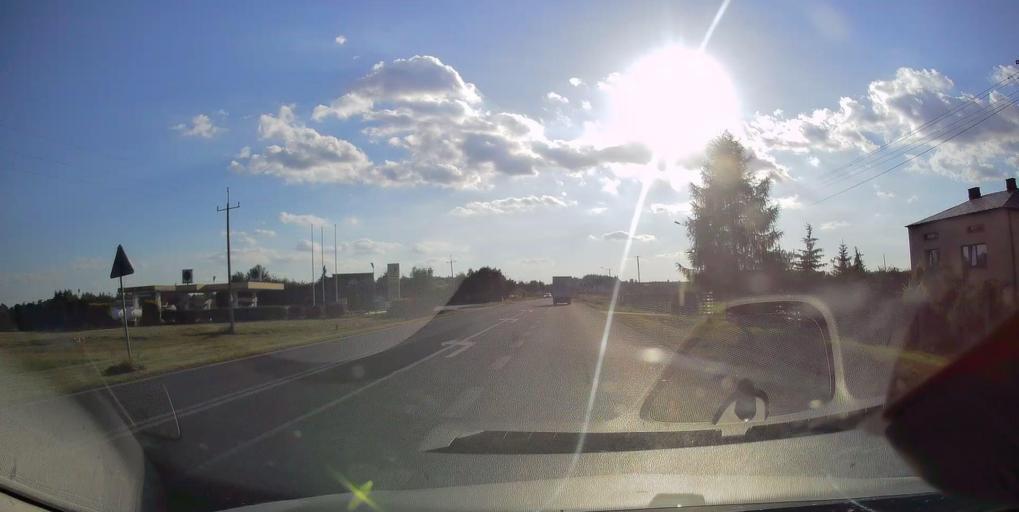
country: PL
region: Lodz Voivodeship
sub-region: Powiat rawski
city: Biala Rawska
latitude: 51.8022
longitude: 20.4515
